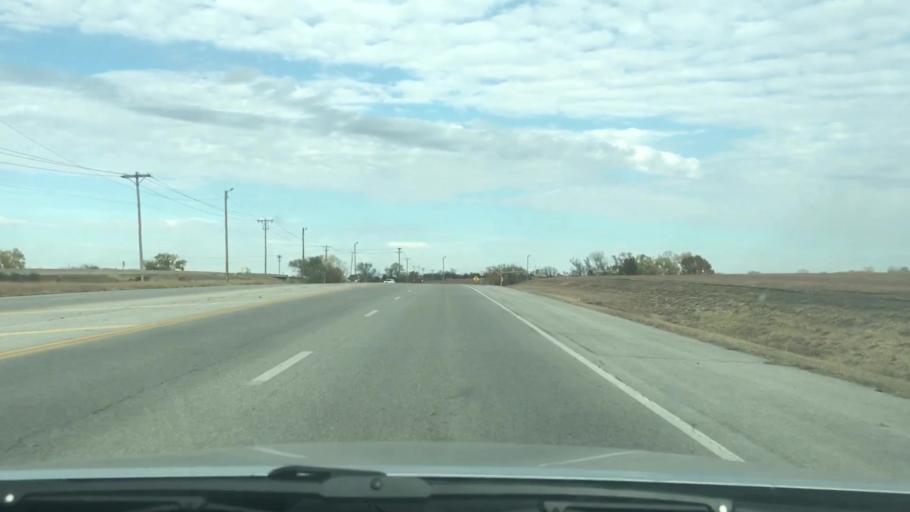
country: US
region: Kansas
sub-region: Sedgwick County
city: Wichita
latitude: 37.6533
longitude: -97.2650
